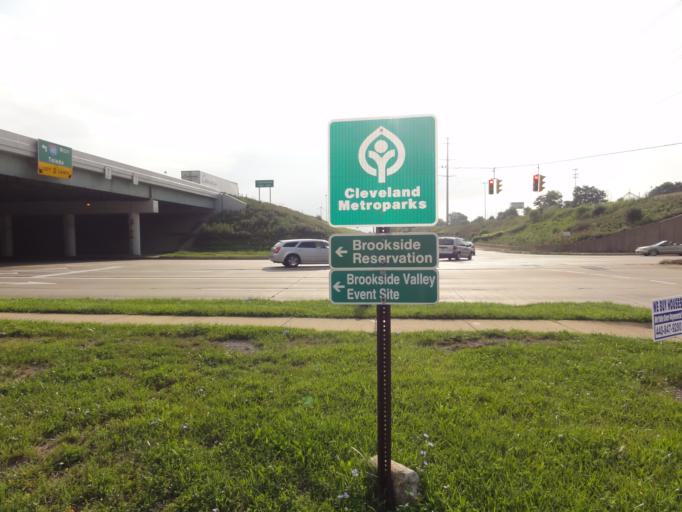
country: US
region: Ohio
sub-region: Cuyahoga County
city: Brooklyn
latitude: 41.4215
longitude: -81.7348
